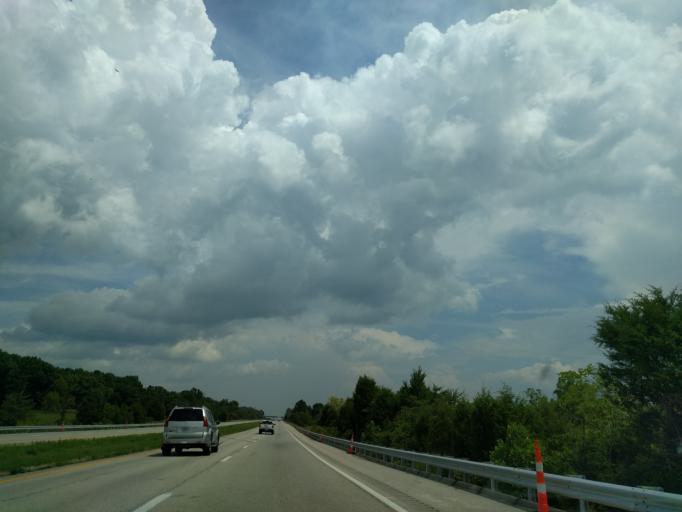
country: US
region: Kentucky
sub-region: Anderson County
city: Lawrenceburg
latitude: 37.9392
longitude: -84.9477
